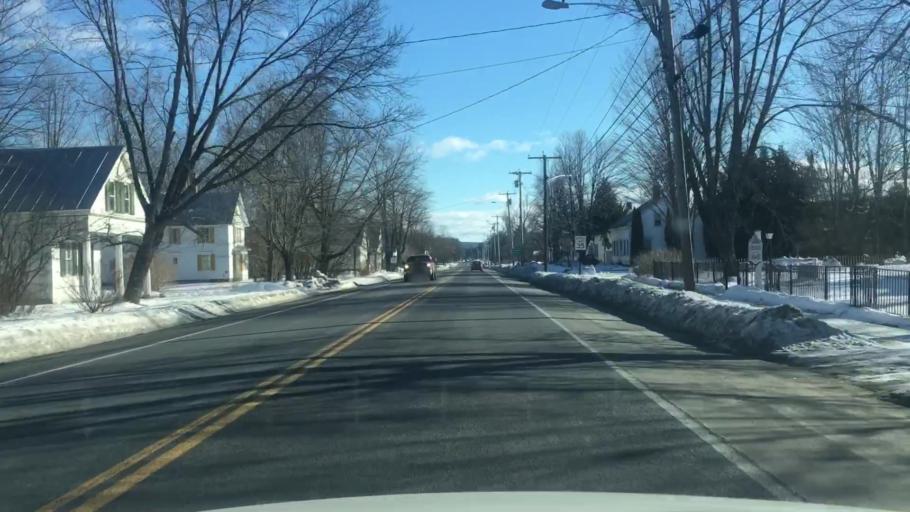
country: US
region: Maine
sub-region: Somerset County
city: Madison
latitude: 44.9489
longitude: -69.8586
